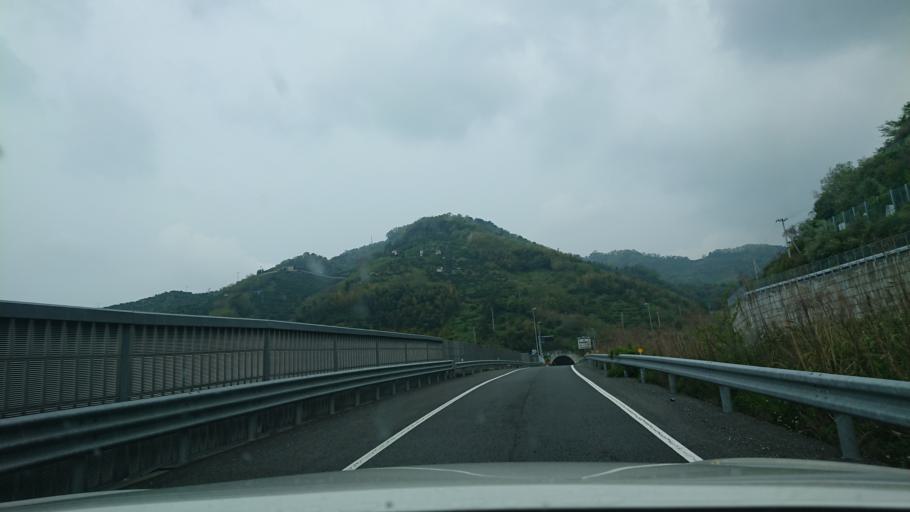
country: JP
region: Ehime
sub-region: Nishiuwa-gun
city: Ikata-cho
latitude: 33.4688
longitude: 132.4264
